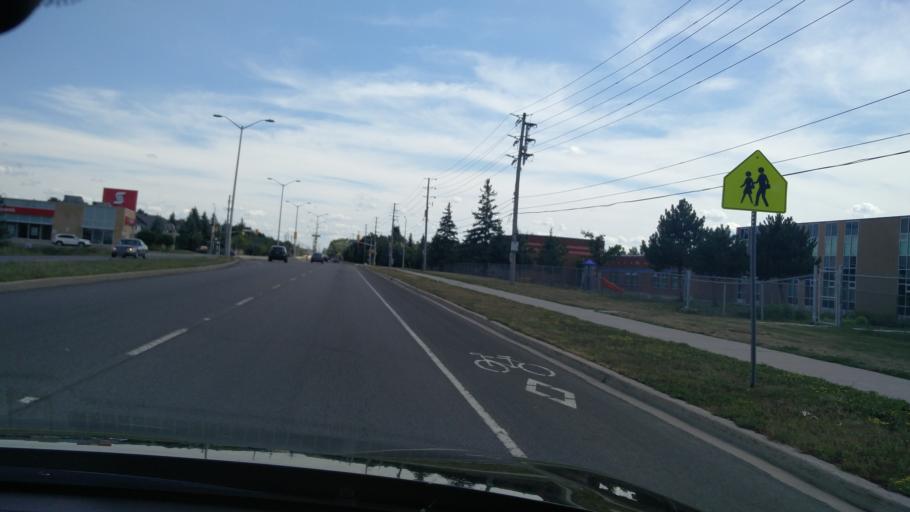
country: CA
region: Ontario
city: Bells Corners
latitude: 45.2894
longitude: -75.7262
